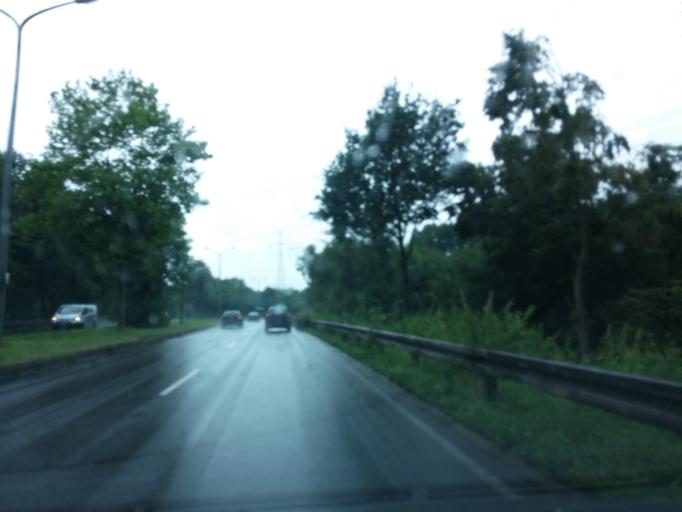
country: DE
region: North Rhine-Westphalia
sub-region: Regierungsbezirk Munster
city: Gladbeck
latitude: 51.5803
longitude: 7.0235
